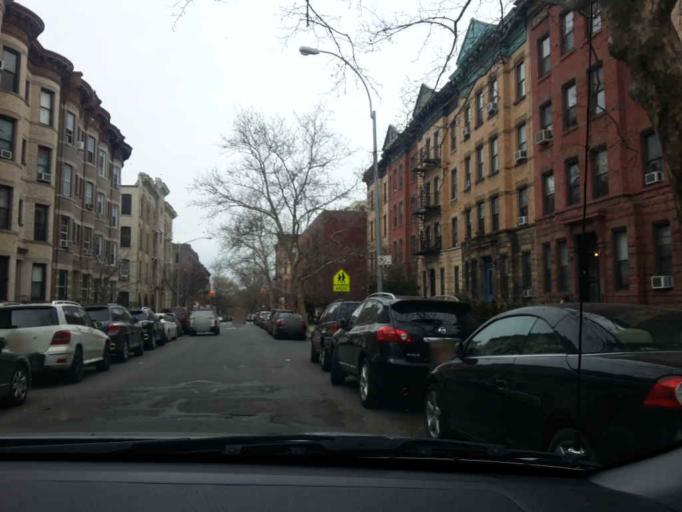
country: US
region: New York
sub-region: Kings County
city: Brooklyn
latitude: 40.6730
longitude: -73.9784
